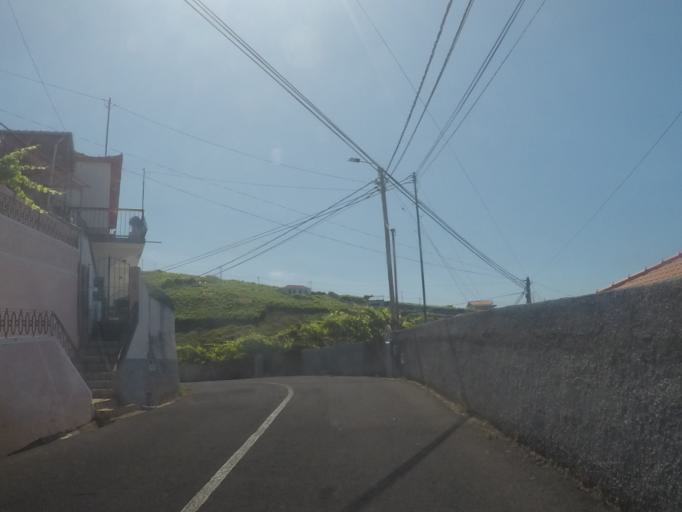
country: PT
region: Madeira
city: Camara de Lobos
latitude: 32.6713
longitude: -16.9697
